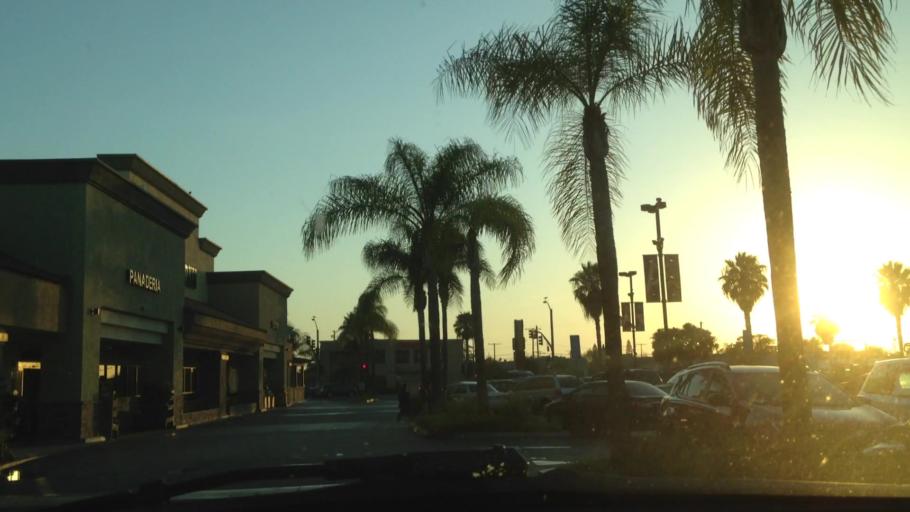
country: US
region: California
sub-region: Orange County
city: Anaheim
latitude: 33.8379
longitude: -117.8880
